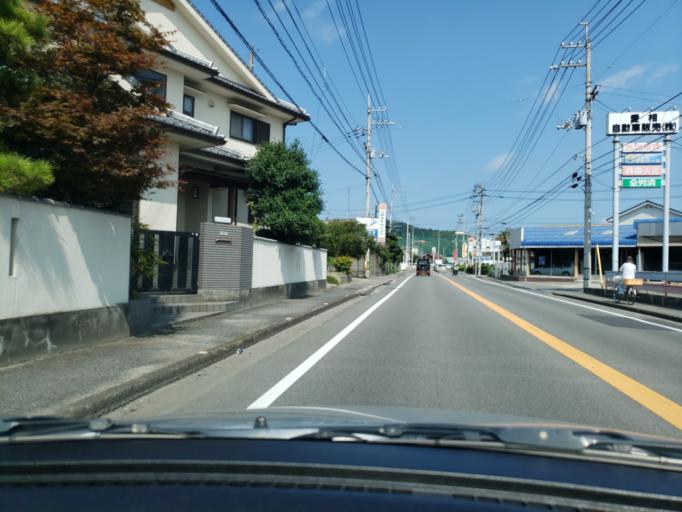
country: JP
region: Ehime
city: Hojo
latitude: 34.0994
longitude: 132.9701
